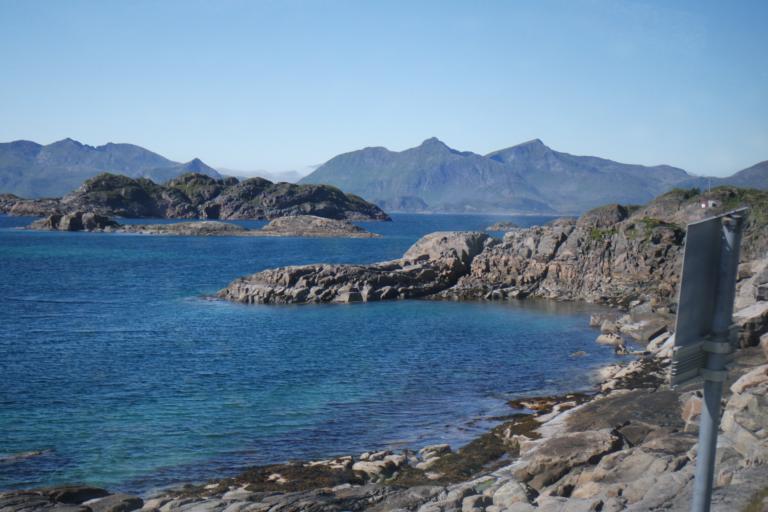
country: NO
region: Nordland
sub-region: Vagan
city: Kabelvag
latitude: 68.1631
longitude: 14.2140
